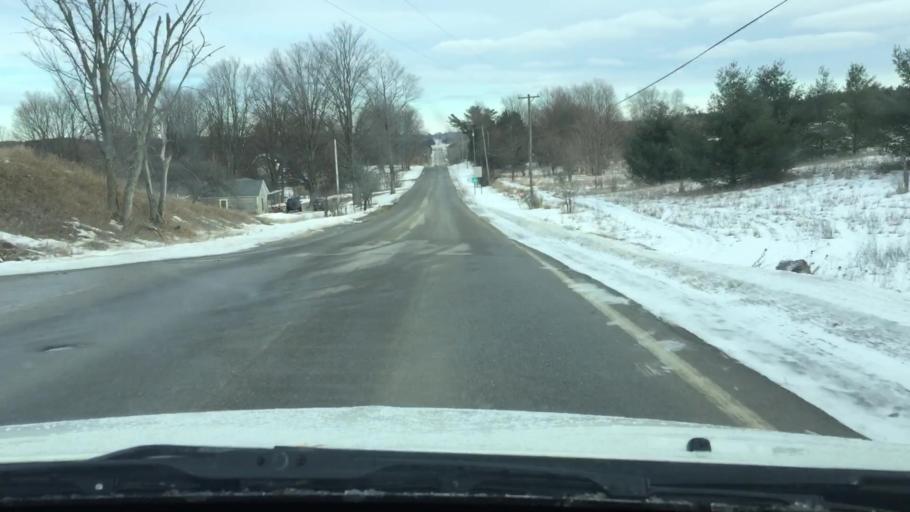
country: US
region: Michigan
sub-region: Wexford County
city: Manton
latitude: 44.4036
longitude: -85.4081
